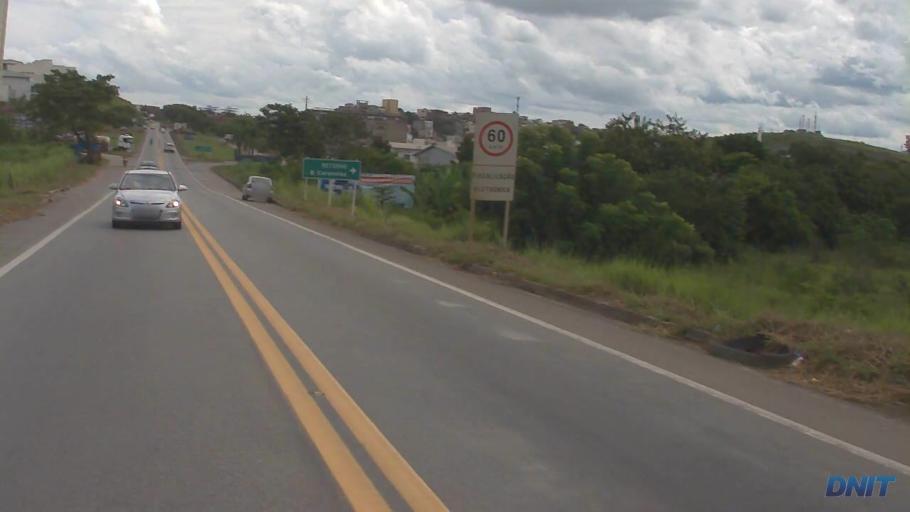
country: BR
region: Minas Gerais
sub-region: Ipatinga
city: Ipatinga
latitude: -19.4533
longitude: -42.5206
